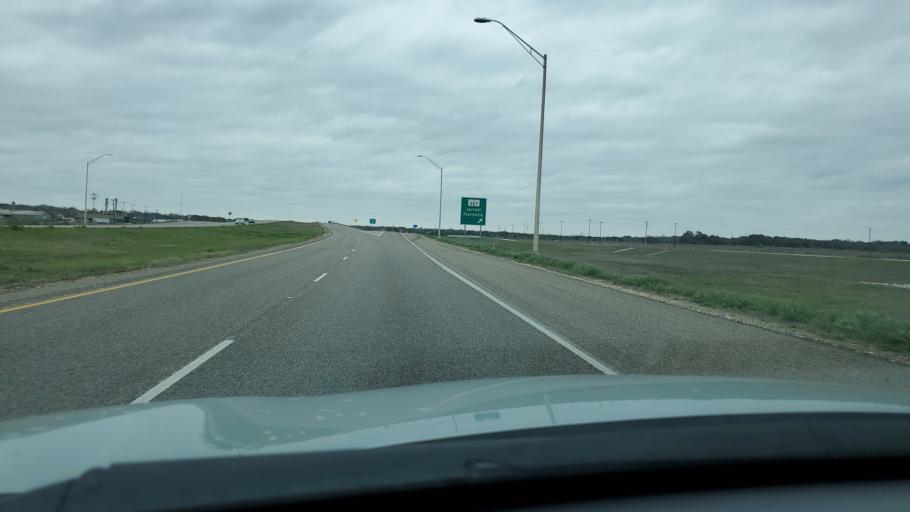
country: US
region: Texas
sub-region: Williamson County
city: Florence
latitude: 30.8389
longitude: -97.7828
